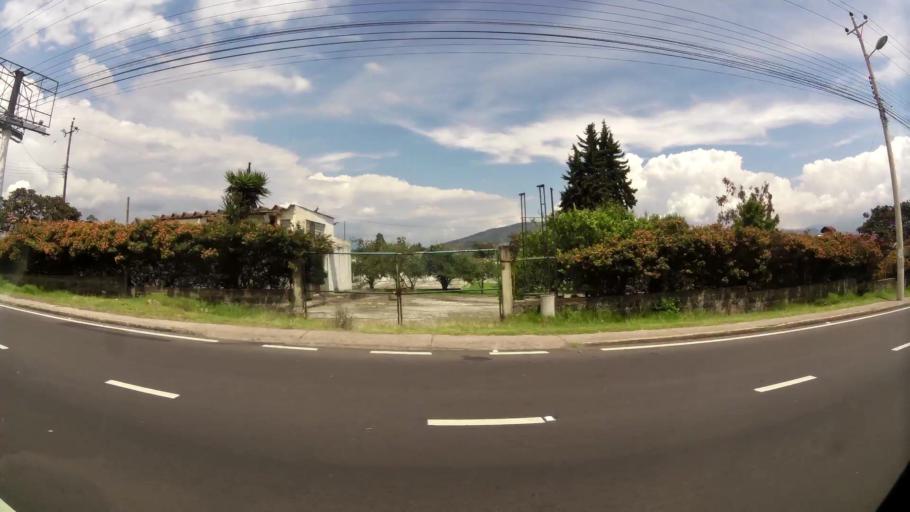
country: EC
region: Pichincha
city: Sangolqui
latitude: -0.2213
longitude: -78.3521
